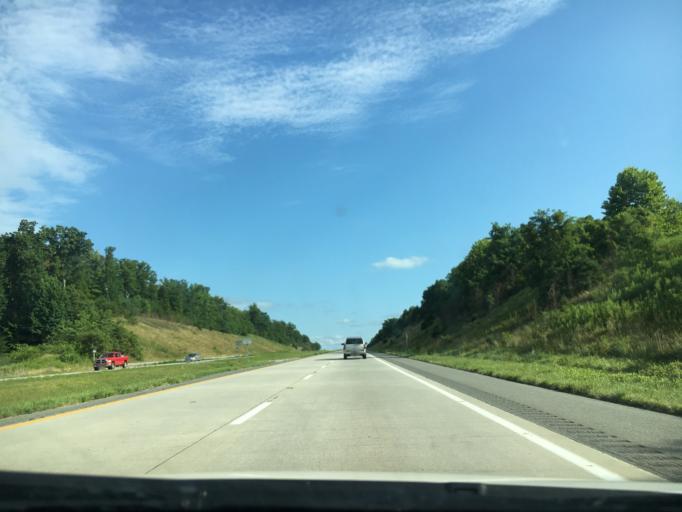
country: US
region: Virginia
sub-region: Amherst County
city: Amherst
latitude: 37.5317
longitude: -79.0659
